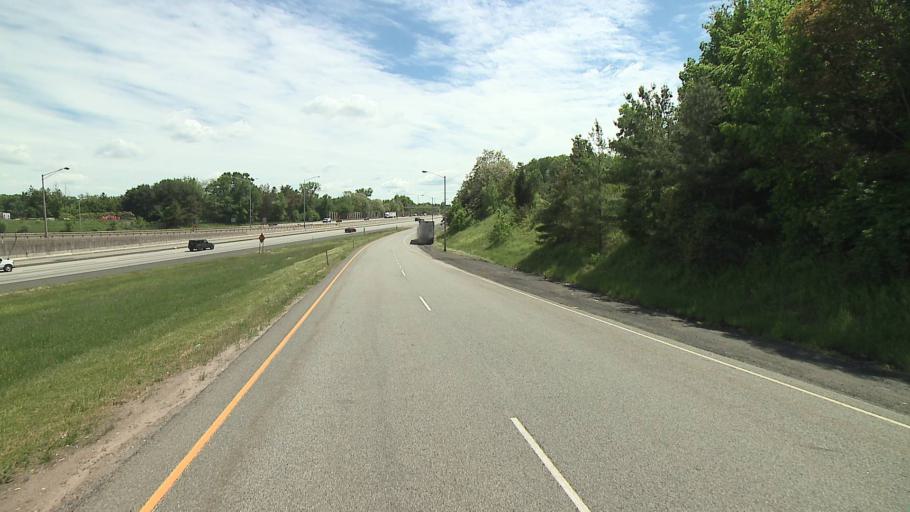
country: US
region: Connecticut
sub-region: Hartford County
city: Windsor
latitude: 41.8517
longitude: -72.6653
